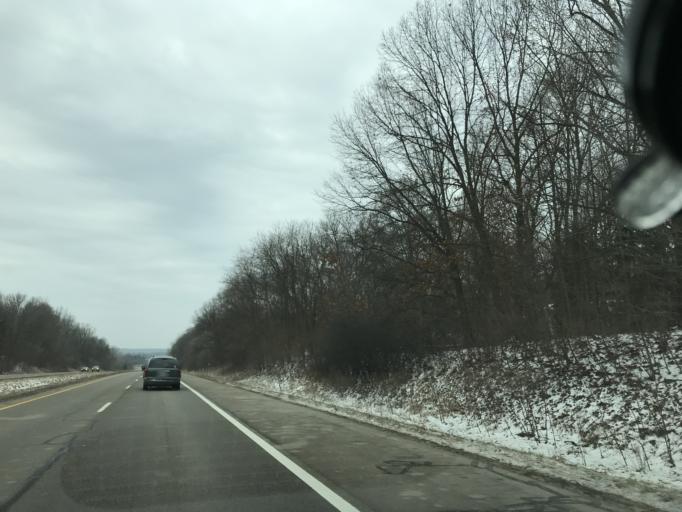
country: US
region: Michigan
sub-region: Kent County
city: Rockford
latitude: 43.0818
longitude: -85.5606
